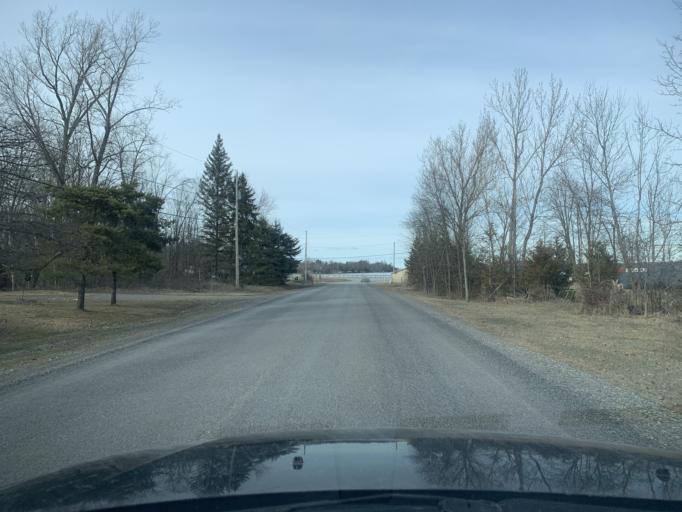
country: CA
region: Ontario
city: Greater Napanee
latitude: 44.4760
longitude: -77.0458
